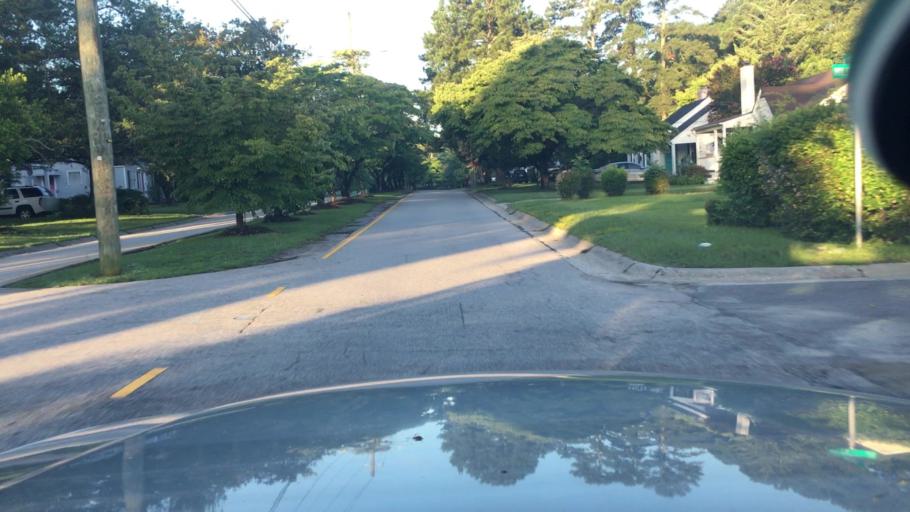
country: US
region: North Carolina
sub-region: Cumberland County
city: Fayetteville
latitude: 35.0656
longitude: -78.9177
